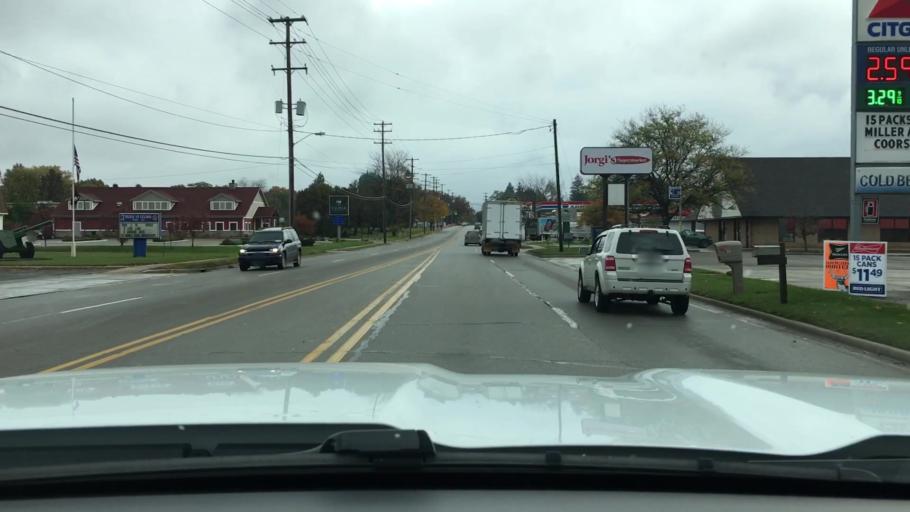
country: US
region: Michigan
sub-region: Montcalm County
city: Greenville
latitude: 43.1772
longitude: -85.2745
